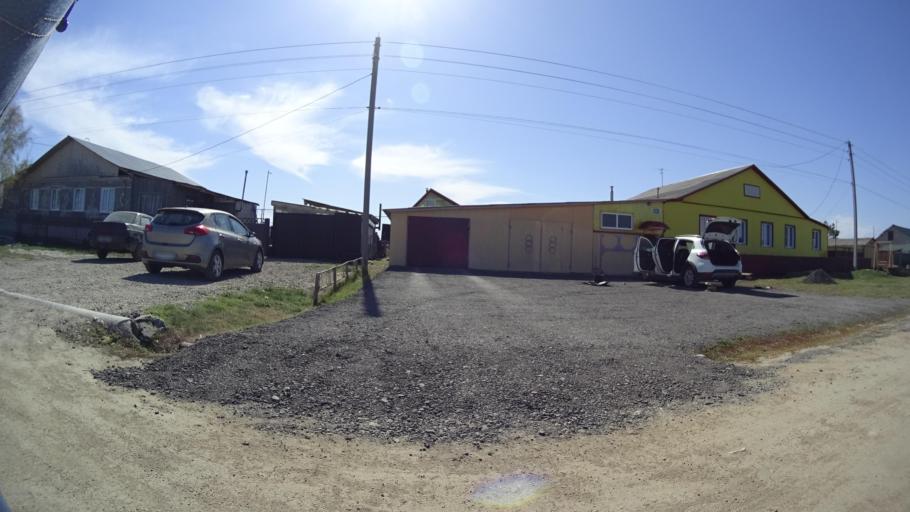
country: RU
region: Chelyabinsk
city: Chesma
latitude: 53.7889
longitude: 61.0384
